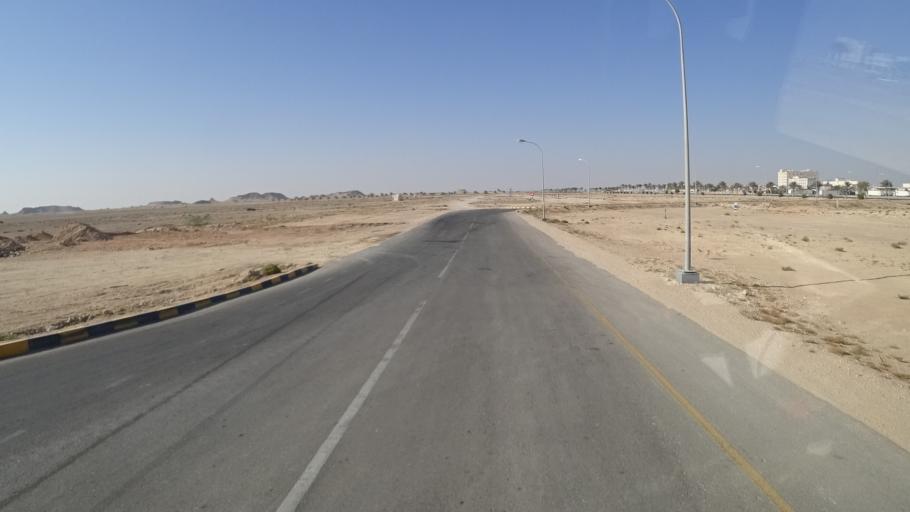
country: OM
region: Zufar
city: Salalah
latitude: 17.6055
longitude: 54.0332
